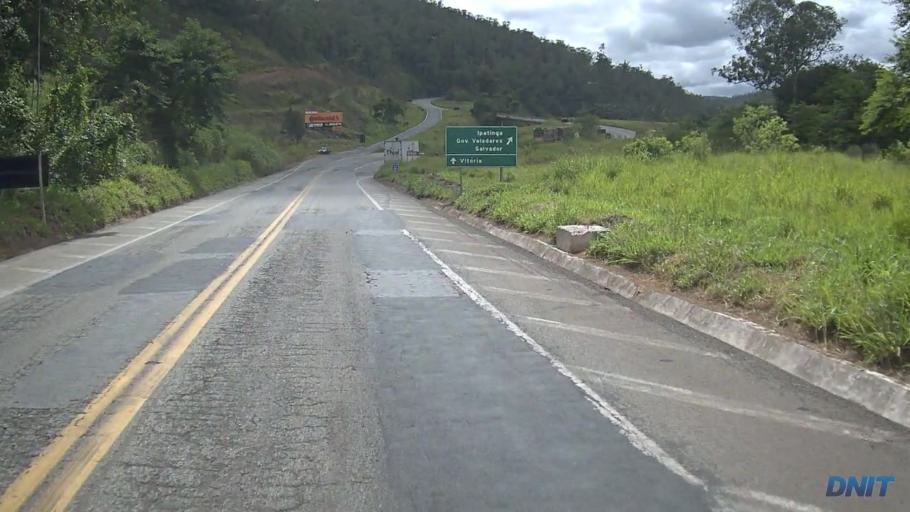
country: BR
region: Minas Gerais
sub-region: Joao Monlevade
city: Joao Monlevade
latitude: -19.8477
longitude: -43.1635
